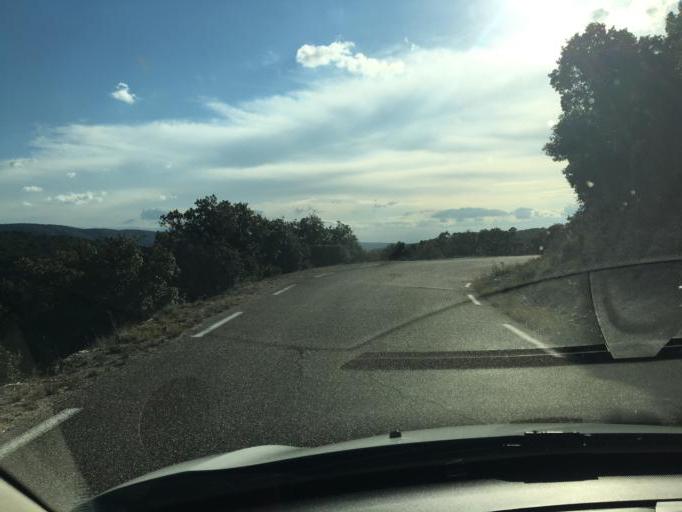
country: FR
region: Provence-Alpes-Cote d'Azur
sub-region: Departement du Vaucluse
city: Villes-sur-Auzon
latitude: 44.0350
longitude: 5.2631
